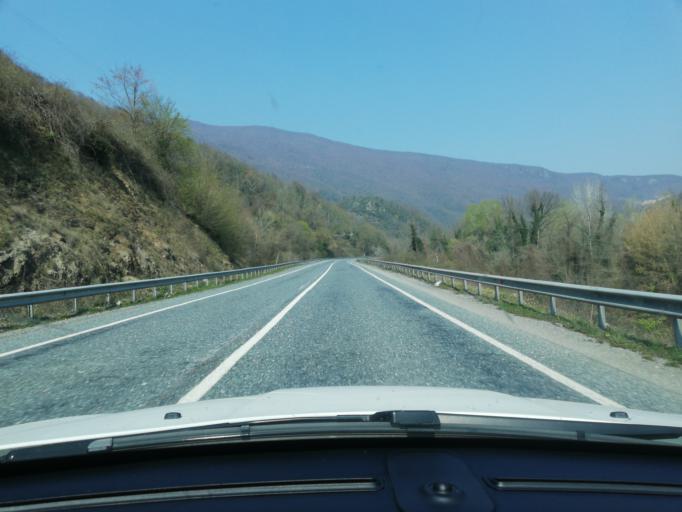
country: TR
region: Zonguldak
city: Gokcebey
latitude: 41.2563
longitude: 32.1597
